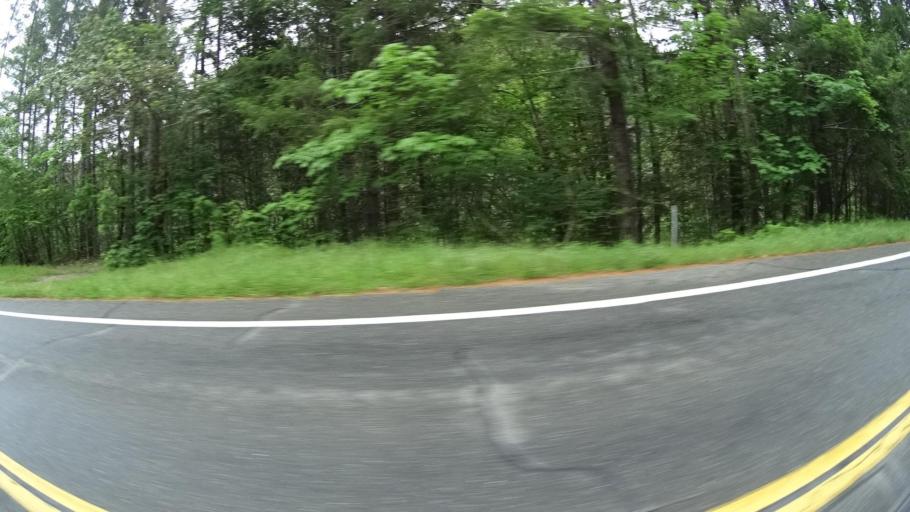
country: US
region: California
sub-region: Humboldt County
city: Willow Creek
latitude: 41.2699
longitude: -123.6057
